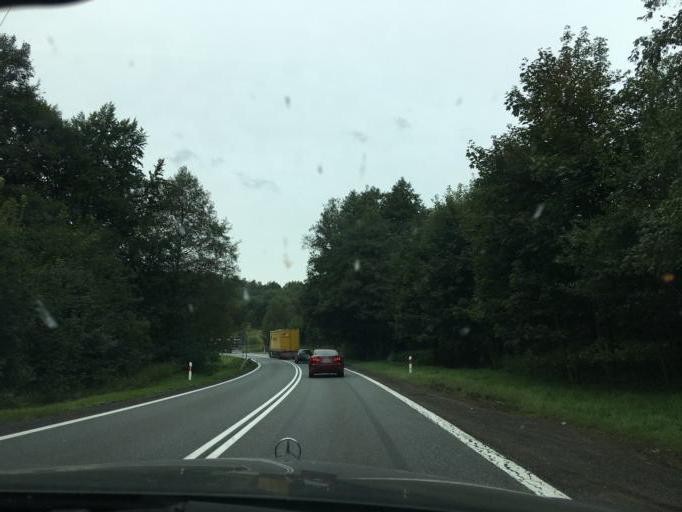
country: PL
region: Lower Silesian Voivodeship
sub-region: Powiat klodzki
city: Lewin Klodzki
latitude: 50.4087
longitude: 16.2970
